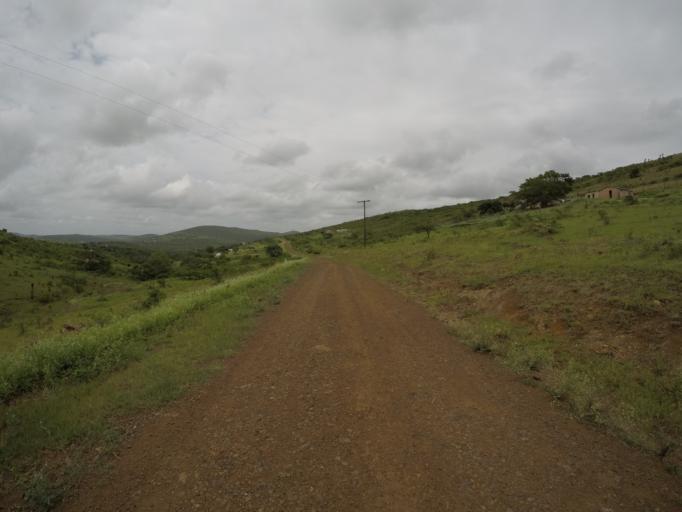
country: ZA
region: KwaZulu-Natal
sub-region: uThungulu District Municipality
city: Empangeni
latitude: -28.6187
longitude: 31.8919
